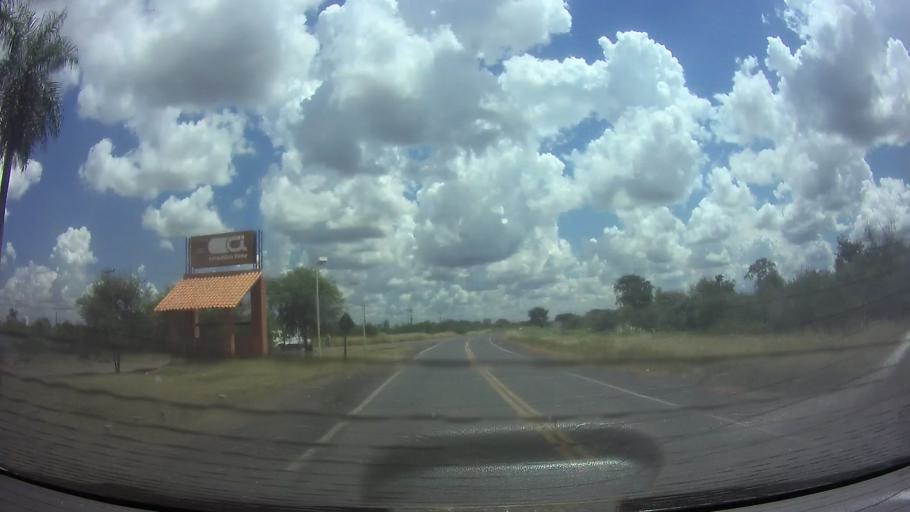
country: PY
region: Central
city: Colonia Mariano Roque Alonso
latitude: -25.1873
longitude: -57.5967
